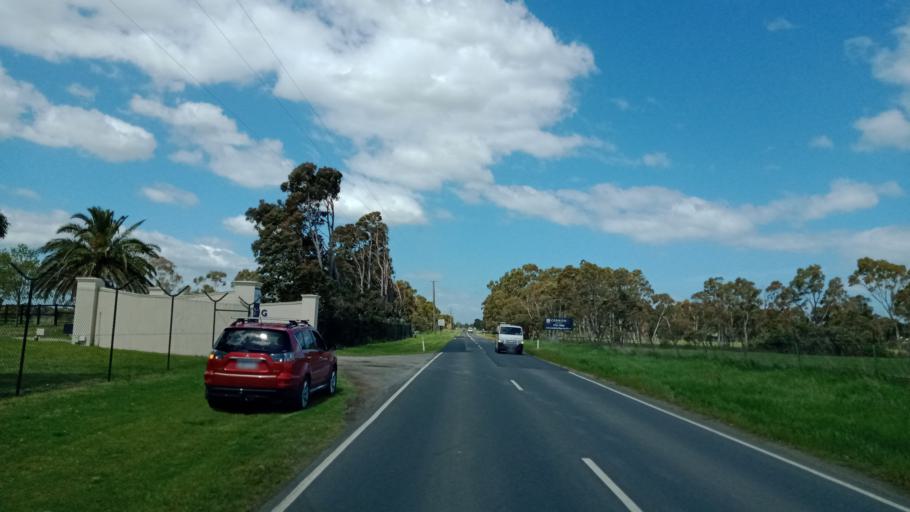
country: AU
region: Victoria
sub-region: Kingston
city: Chelsea Heights
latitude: -38.0459
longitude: 145.1490
